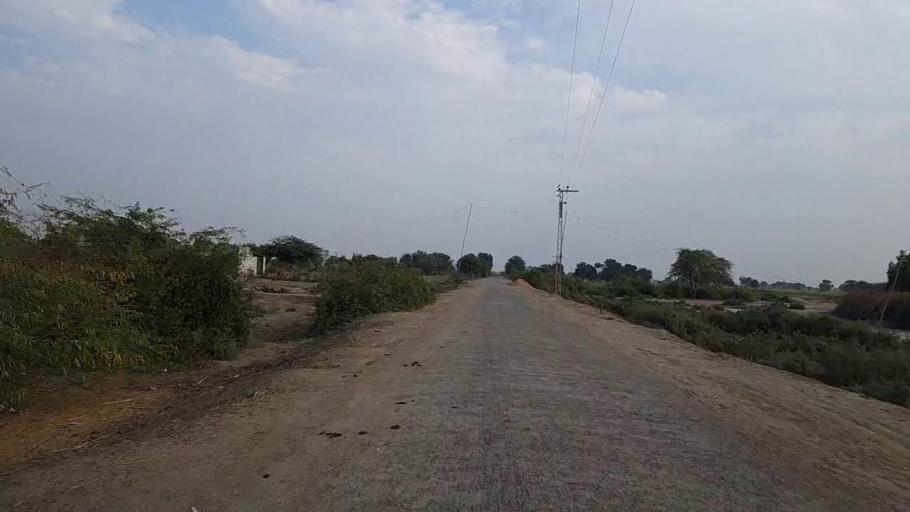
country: PK
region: Sindh
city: Pithoro
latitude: 25.4580
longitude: 69.2782
